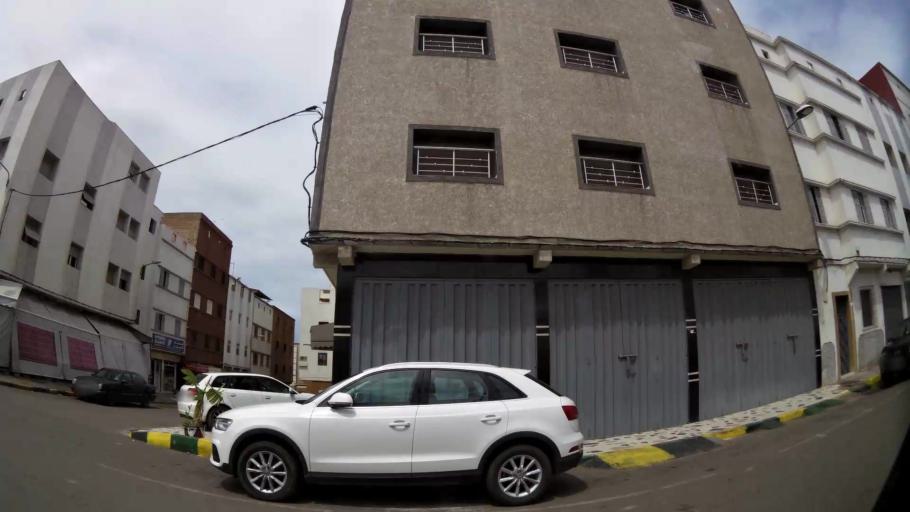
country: MA
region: Grand Casablanca
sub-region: Mediouna
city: Tit Mellil
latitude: 33.6030
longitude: -7.5111
